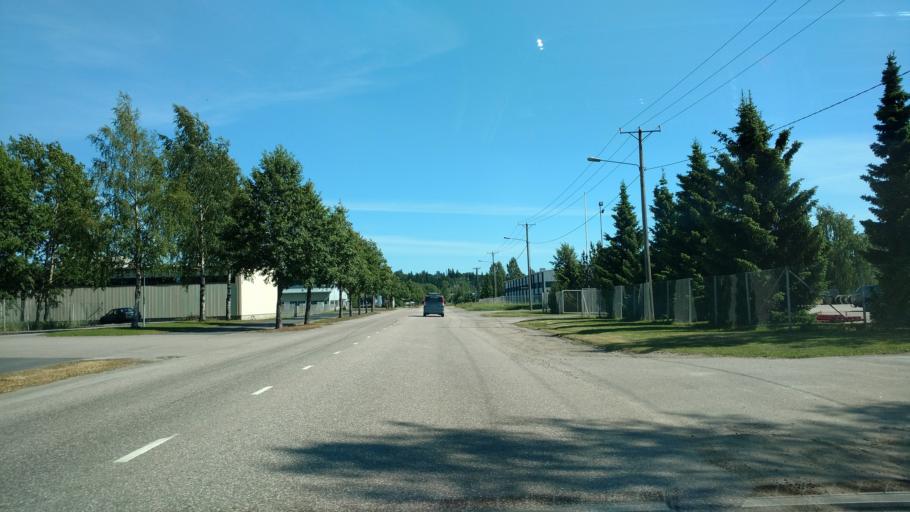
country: FI
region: Varsinais-Suomi
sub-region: Salo
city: Salo
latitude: 60.3829
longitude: 23.1099
